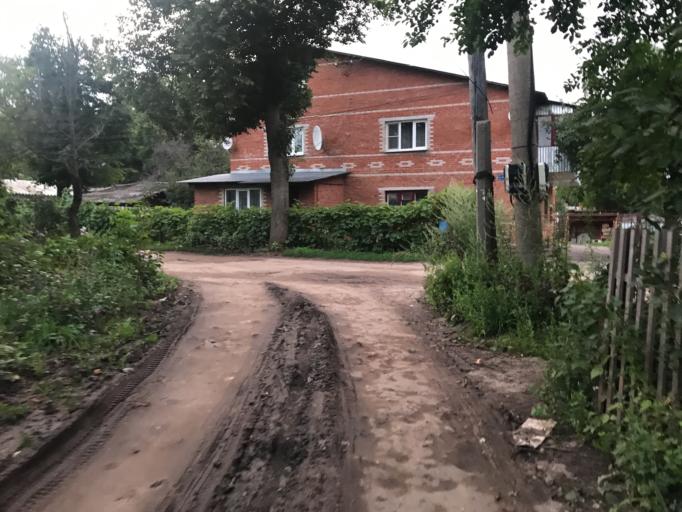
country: RU
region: Tula
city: Priupskiy
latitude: 53.9370
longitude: 37.7041
